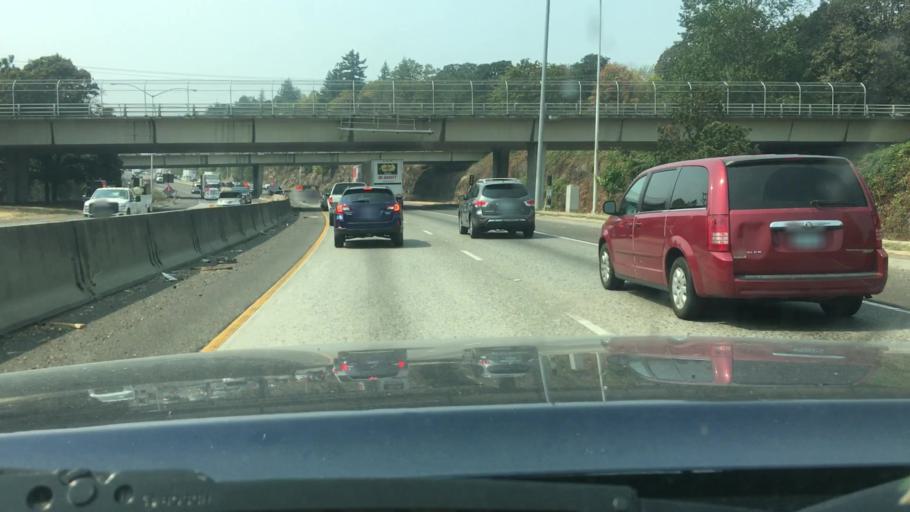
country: US
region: Oregon
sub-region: Clackamas County
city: West Linn
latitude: 45.3623
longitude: -122.6112
